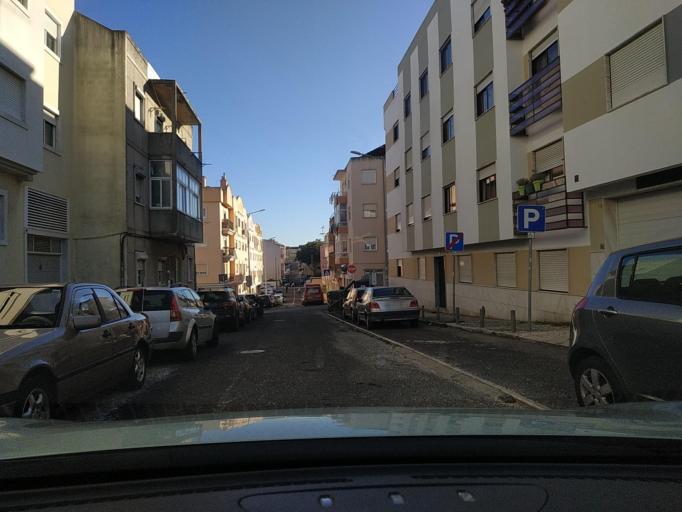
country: PT
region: Lisbon
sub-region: Odivelas
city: Famoes
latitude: 38.7702
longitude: -9.2192
